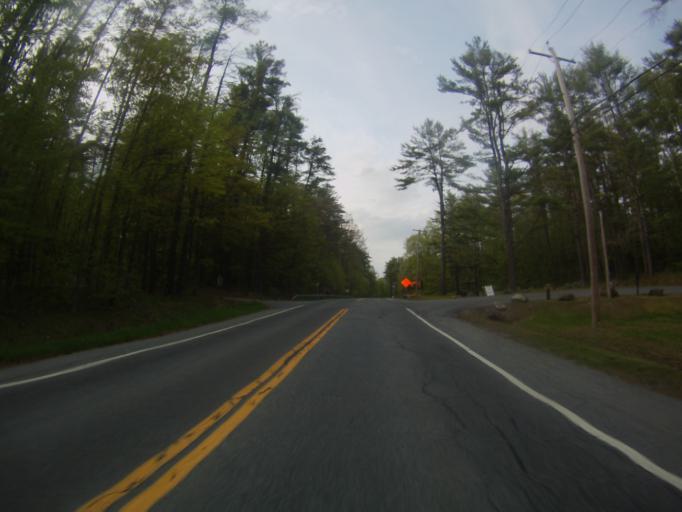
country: US
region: New York
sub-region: Essex County
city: Ticonderoga
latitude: 43.7926
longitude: -73.4870
